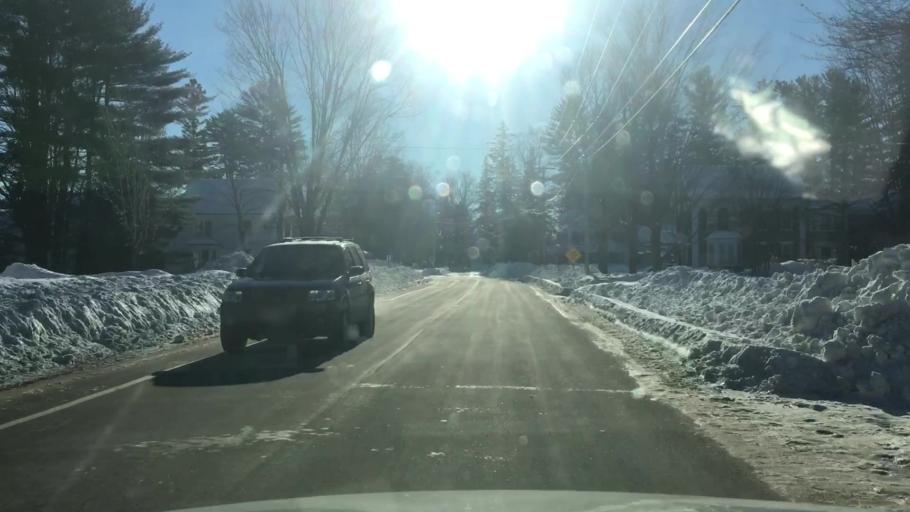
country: US
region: Maine
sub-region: Oxford County
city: Bethel
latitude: 44.4018
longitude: -70.7889
